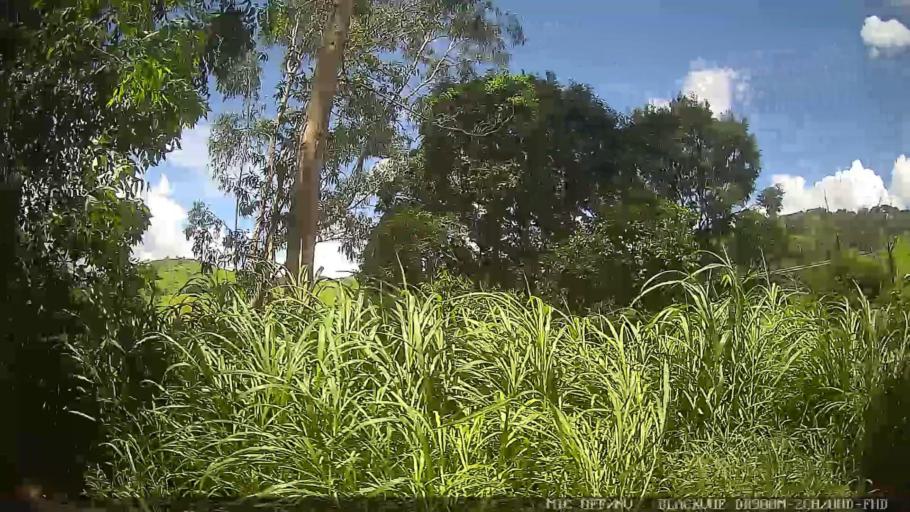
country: BR
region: Minas Gerais
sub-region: Extrema
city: Extrema
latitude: -22.7646
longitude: -46.4368
